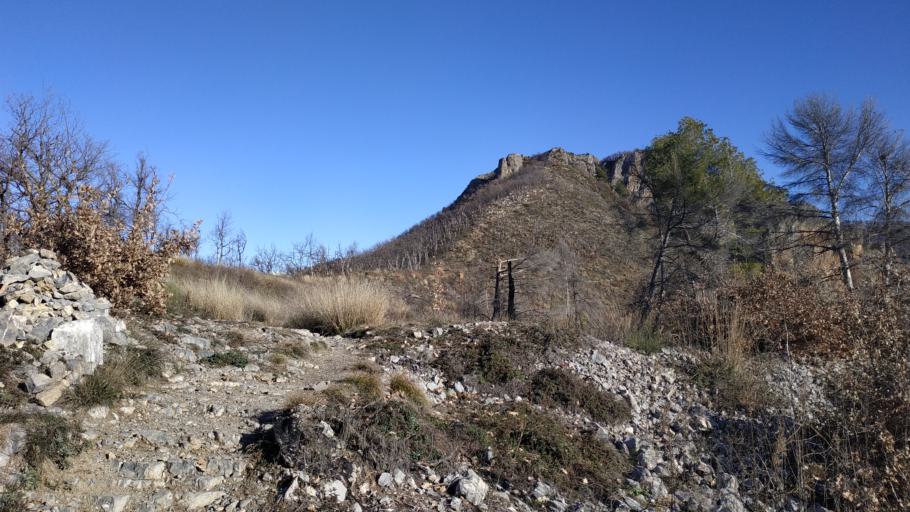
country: FR
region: Provence-Alpes-Cote d'Azur
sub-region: Departement des Alpes-de-Haute-Provence
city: Digne-les-Bains
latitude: 44.0941
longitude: 6.2433
